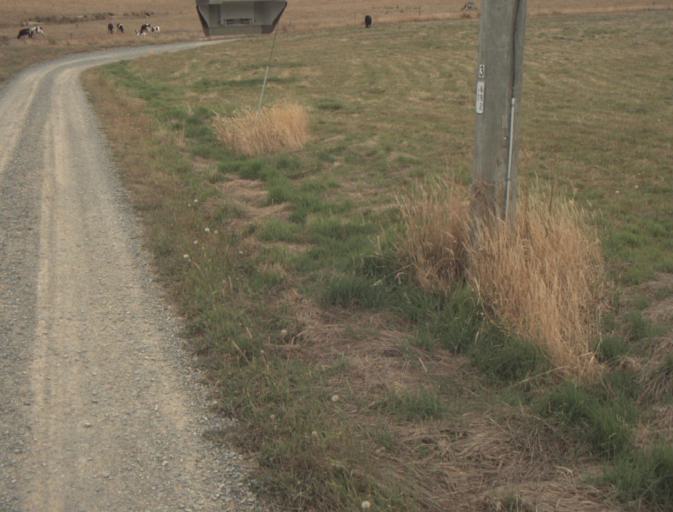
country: AU
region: Tasmania
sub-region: Launceston
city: Mayfield
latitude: -41.2410
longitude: 147.2060
